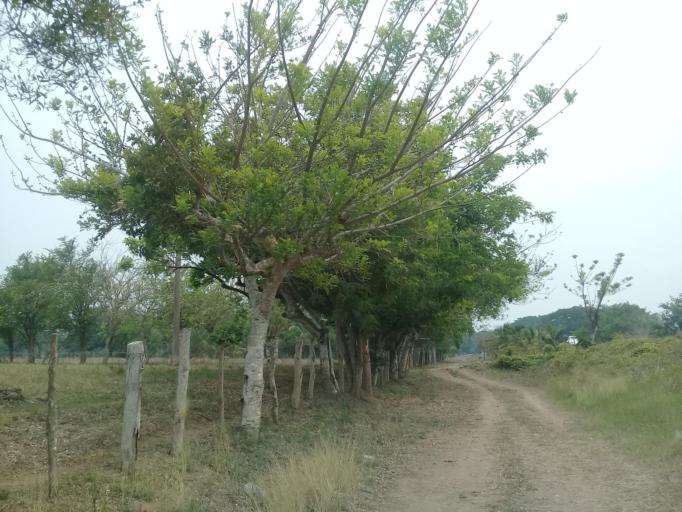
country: MX
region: Veracruz
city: Jamapa
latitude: 18.9478
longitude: -96.1978
